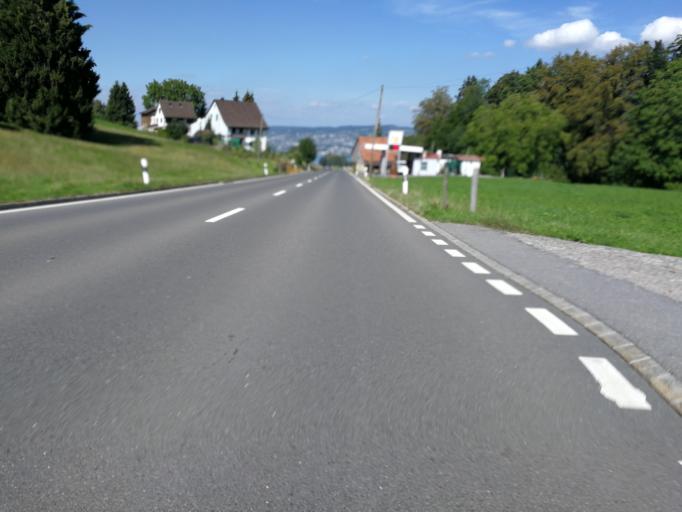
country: CH
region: Zurich
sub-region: Bezirk Horgen
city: Horgen / Allmend
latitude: 47.2320
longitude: 8.6142
